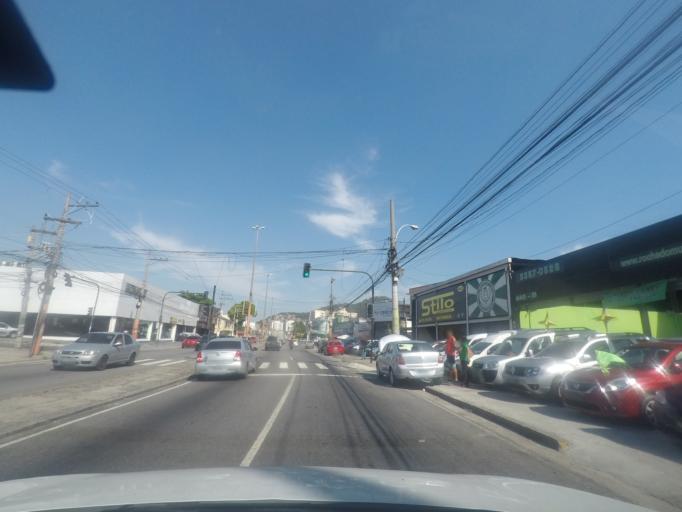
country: BR
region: Rio de Janeiro
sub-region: Sao Joao De Meriti
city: Sao Joao de Meriti
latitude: -22.8806
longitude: -43.3538
